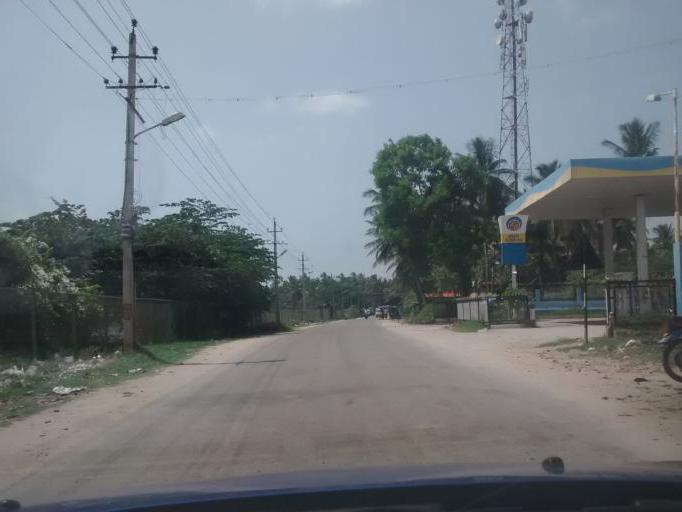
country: IN
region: Karnataka
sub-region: Hassan
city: Konanur
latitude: 12.5622
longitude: 76.2649
